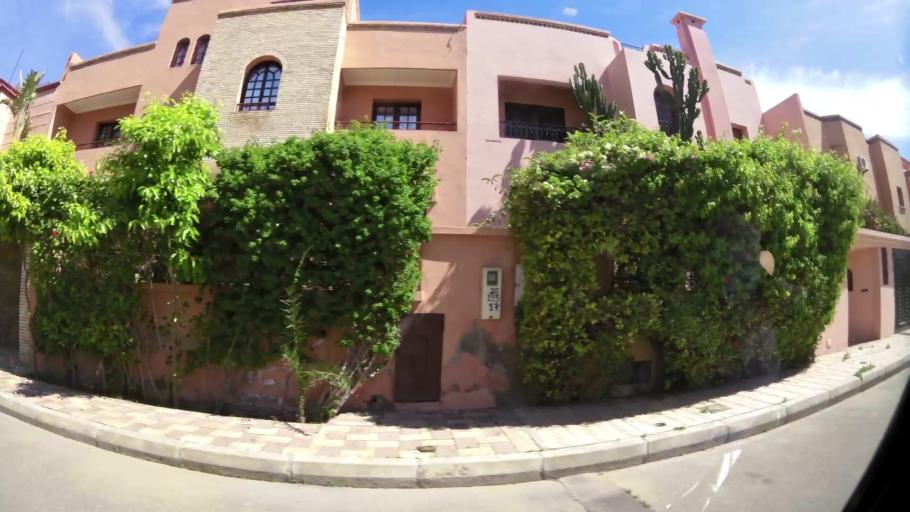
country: MA
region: Marrakech-Tensift-Al Haouz
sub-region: Marrakech
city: Marrakesh
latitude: 31.6760
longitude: -8.0021
